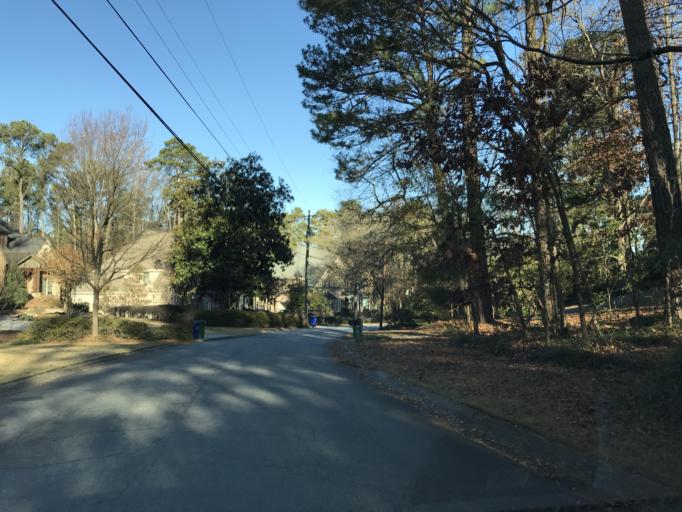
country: US
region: Georgia
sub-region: DeKalb County
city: North Atlanta
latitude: 33.8858
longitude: -84.3391
